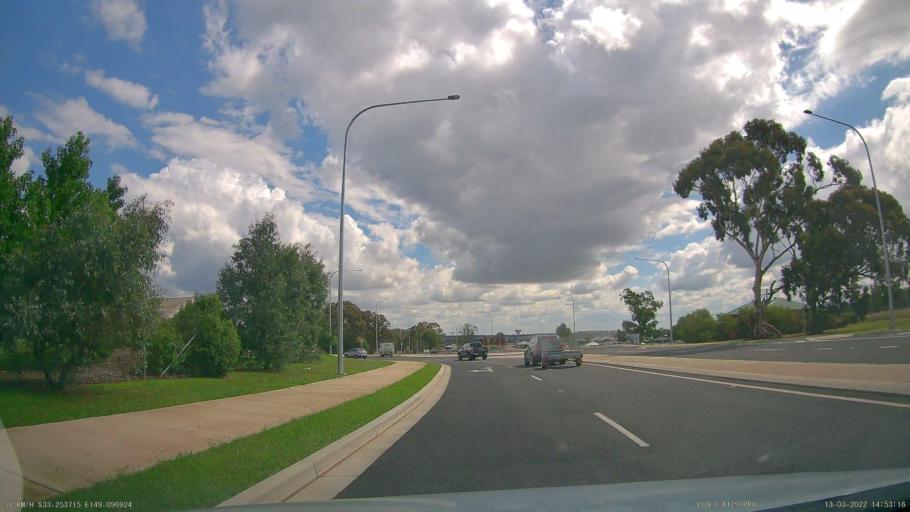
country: AU
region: New South Wales
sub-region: Orange Municipality
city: Orange
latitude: -33.2539
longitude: 149.0969
